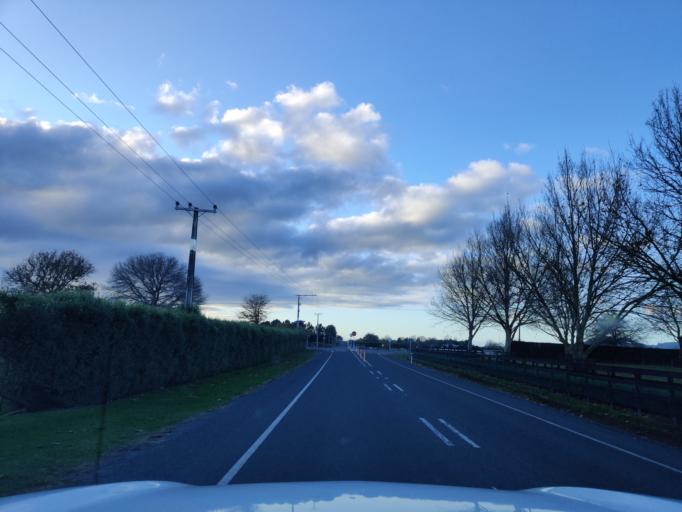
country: NZ
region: Waikato
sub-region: Waipa District
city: Cambridge
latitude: -37.8758
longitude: 175.4389
